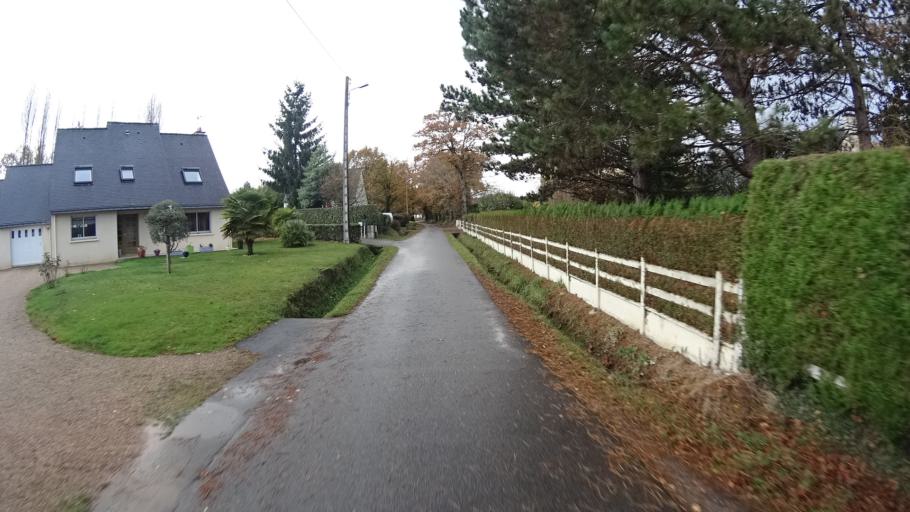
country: FR
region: Brittany
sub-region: Departement d'Ille-et-Vilaine
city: Redon
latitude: 47.6717
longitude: -2.0753
